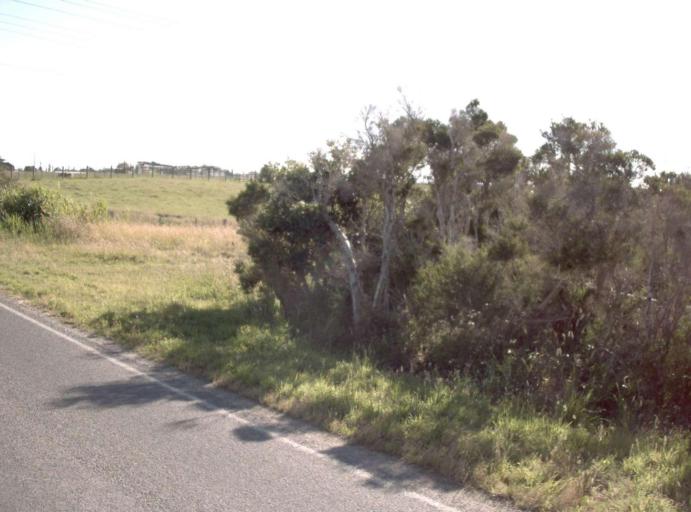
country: AU
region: Victoria
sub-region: Latrobe
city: Morwell
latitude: -38.6738
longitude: 146.3951
